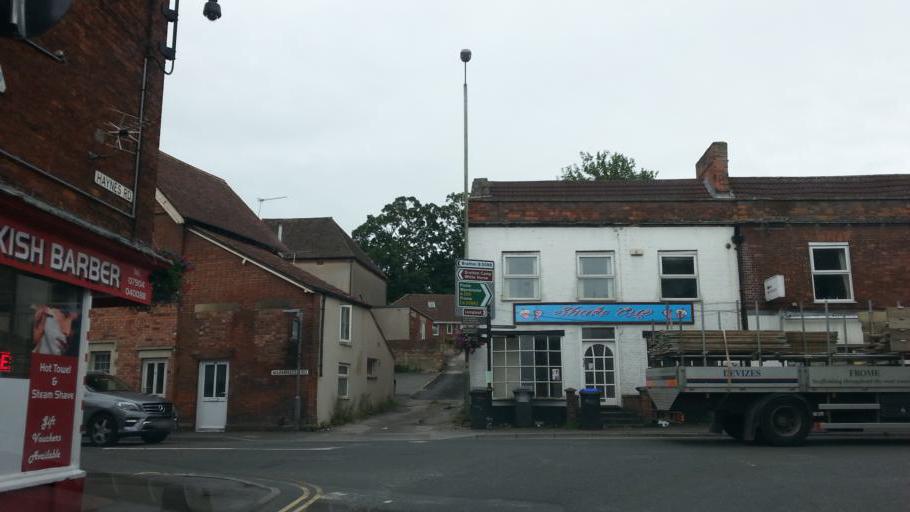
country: GB
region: England
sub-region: Wiltshire
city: Westbury
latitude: 51.2591
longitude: -2.1839
